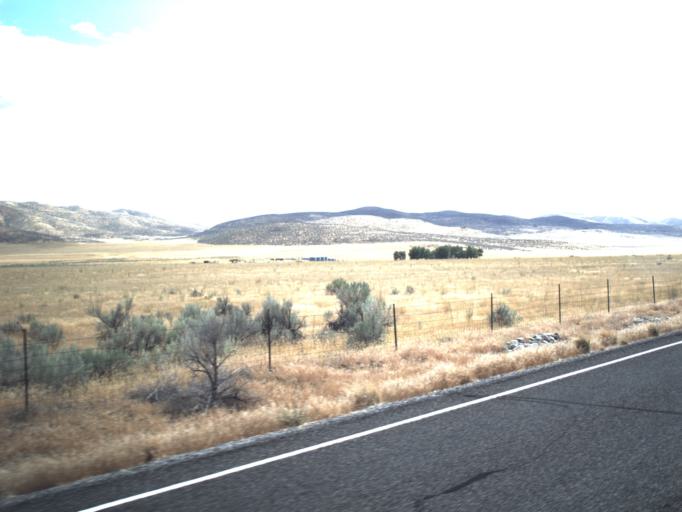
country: US
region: Utah
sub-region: Box Elder County
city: Garland
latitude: 41.8058
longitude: -112.4165
